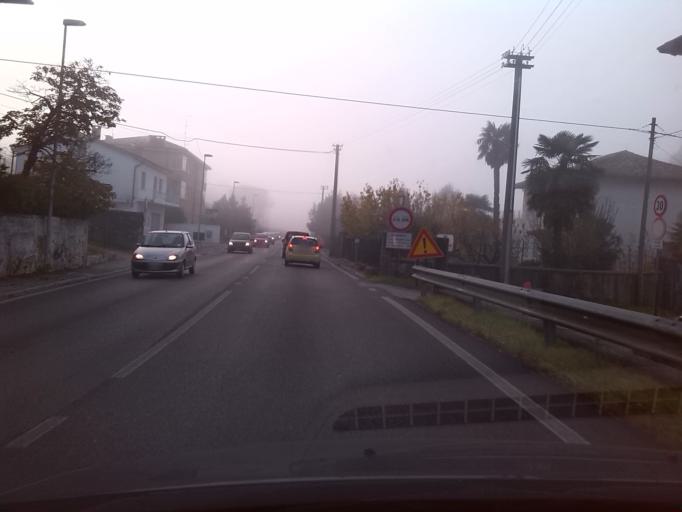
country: IT
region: Friuli Venezia Giulia
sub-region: Provincia di Gorizia
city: Fogliano
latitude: 45.8693
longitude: 13.4803
